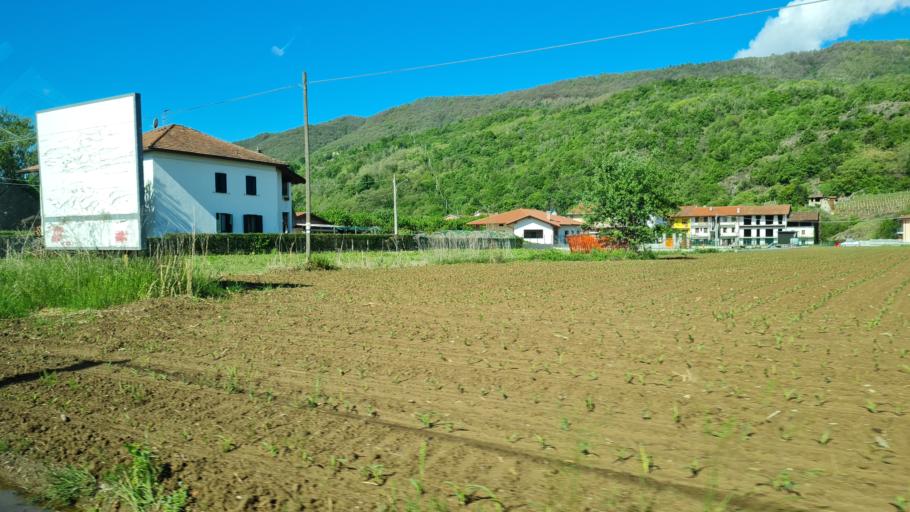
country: IT
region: Piedmont
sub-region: Provincia di Torino
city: Loranze
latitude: 45.4470
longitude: 7.8138
